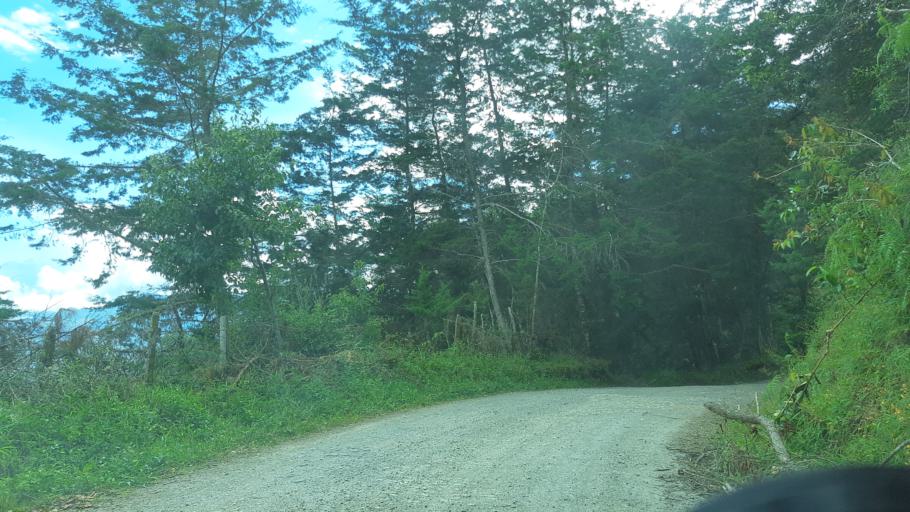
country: CO
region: Boyaca
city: Garagoa
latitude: 5.0499
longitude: -73.3538
